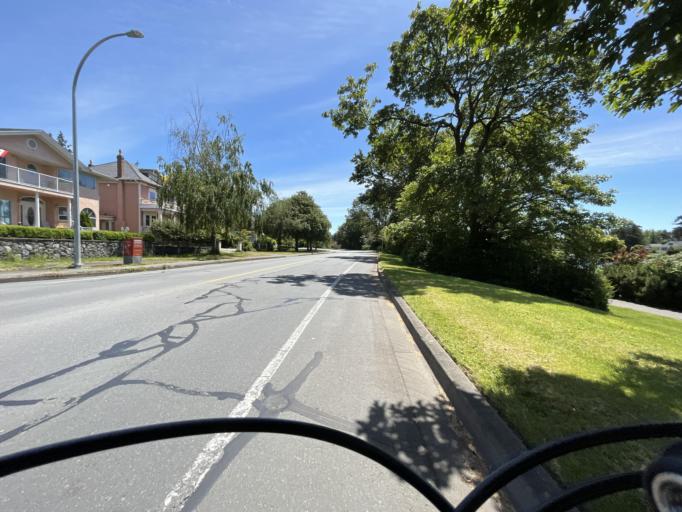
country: CA
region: British Columbia
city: Victoria
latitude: 48.4499
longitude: -123.4085
